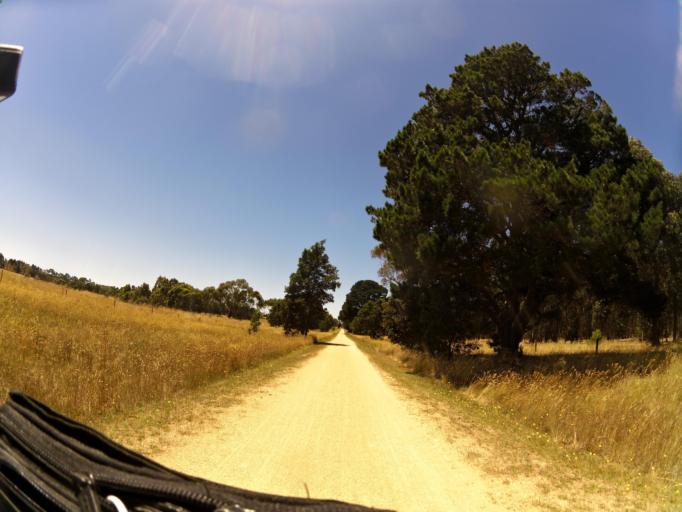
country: AU
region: Victoria
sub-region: Ballarat North
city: Delacombe
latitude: -37.5560
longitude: 143.7477
